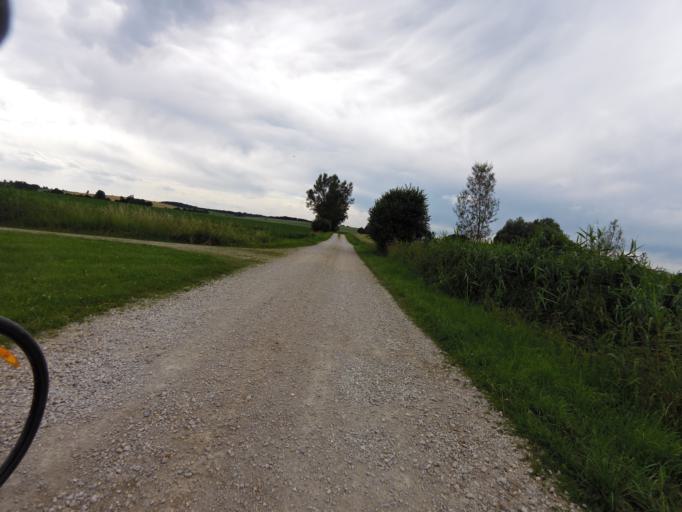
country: DE
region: Bavaria
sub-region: Upper Bavaria
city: Fahrenzhausen
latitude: 48.3712
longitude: 11.5785
